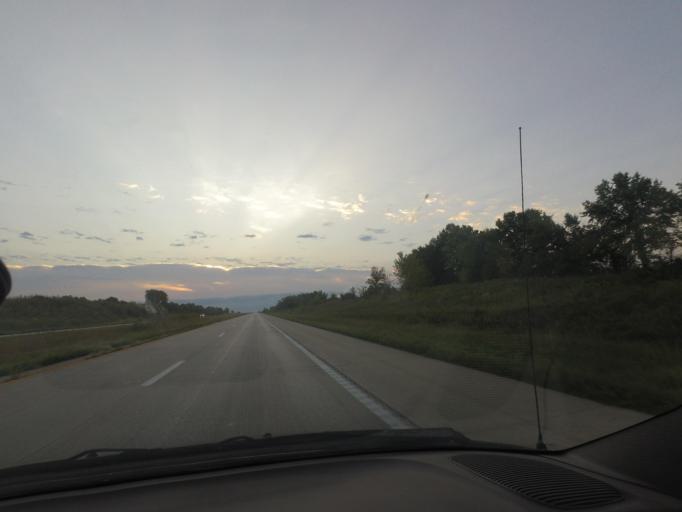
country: US
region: Missouri
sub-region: Macon County
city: Macon
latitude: 39.7518
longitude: -92.3967
